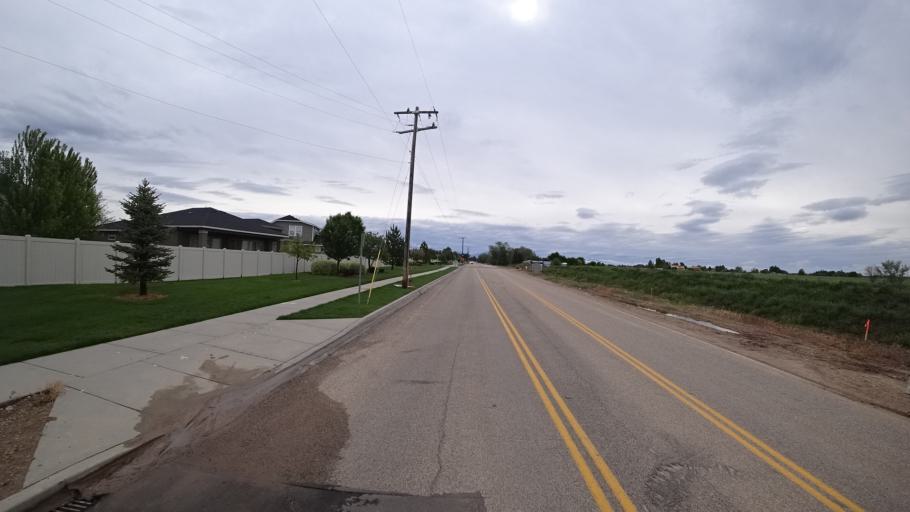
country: US
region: Idaho
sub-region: Ada County
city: Star
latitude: 43.7176
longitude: -116.4981
